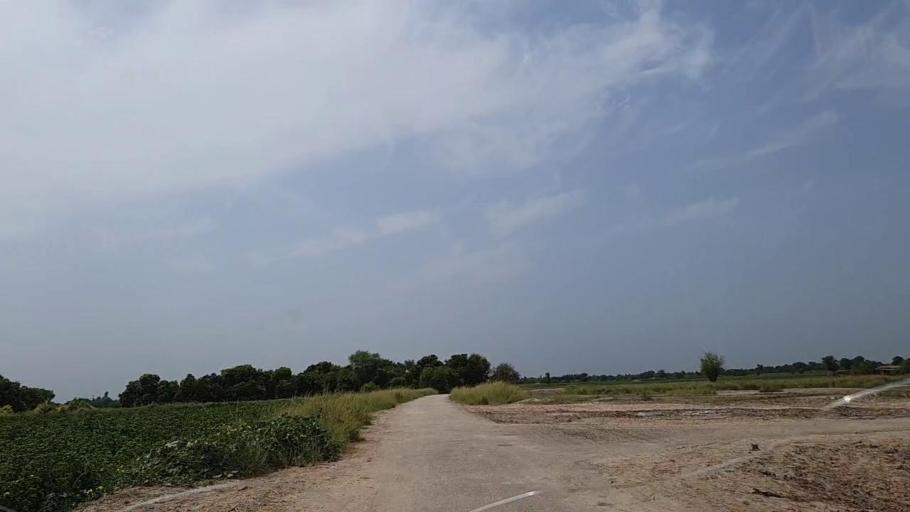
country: PK
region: Sindh
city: Tharu Shah
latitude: 26.8947
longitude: 68.0797
